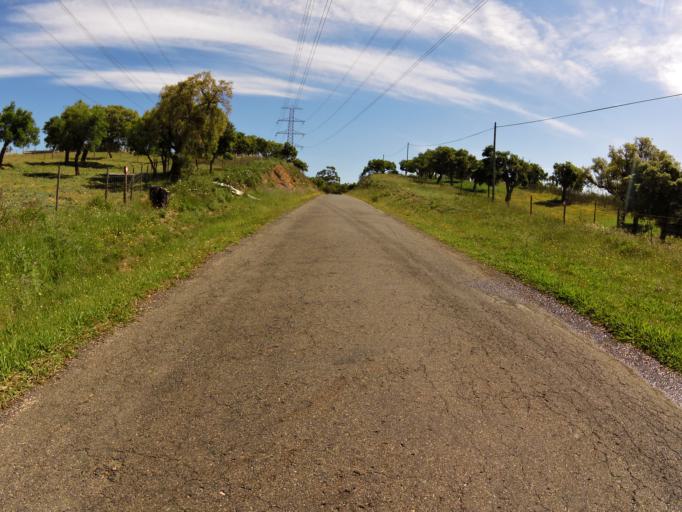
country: PT
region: Setubal
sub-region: Sines
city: Porto Covo
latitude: 37.9350
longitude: -8.7578
